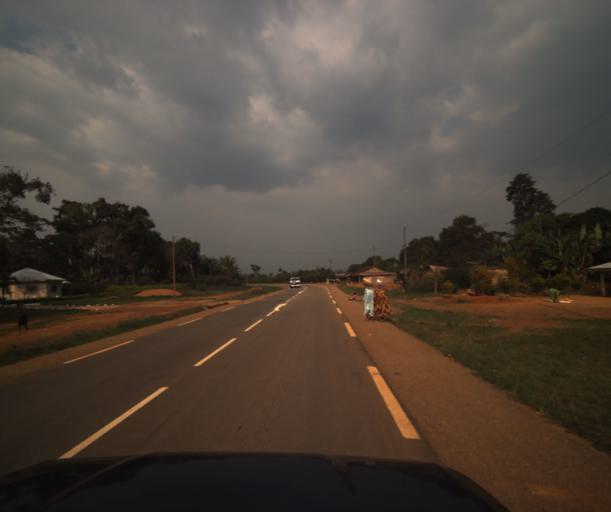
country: CM
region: Centre
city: Mbankomo
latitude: 3.7259
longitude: 11.3902
